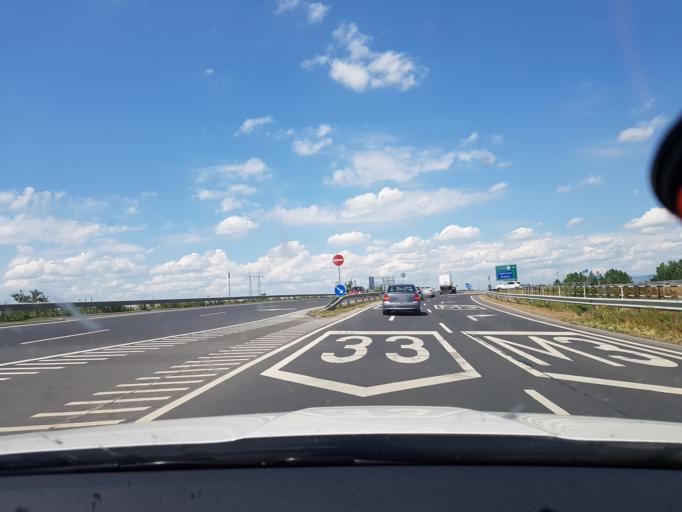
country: HU
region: Heves
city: Fuzesabony
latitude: 47.7287
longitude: 20.4142
